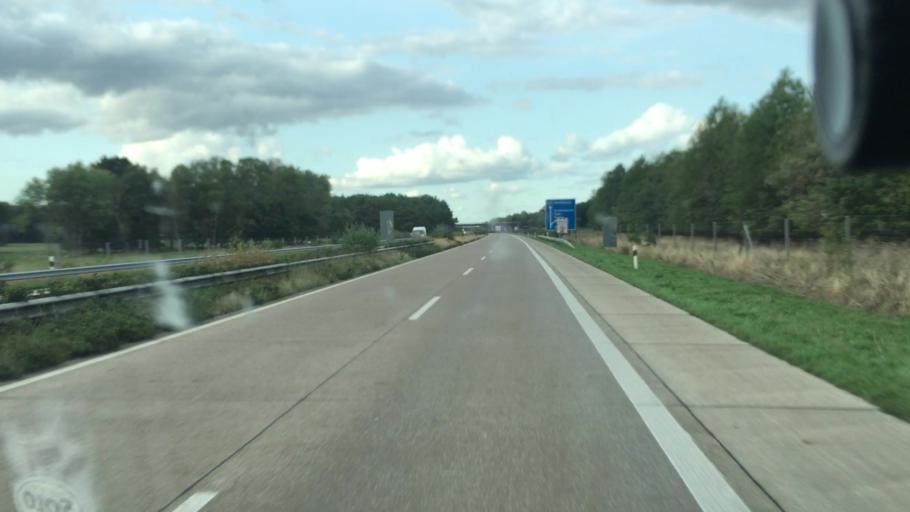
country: DE
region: Lower Saxony
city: Grossenkneten
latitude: 52.9407
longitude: 8.1782
